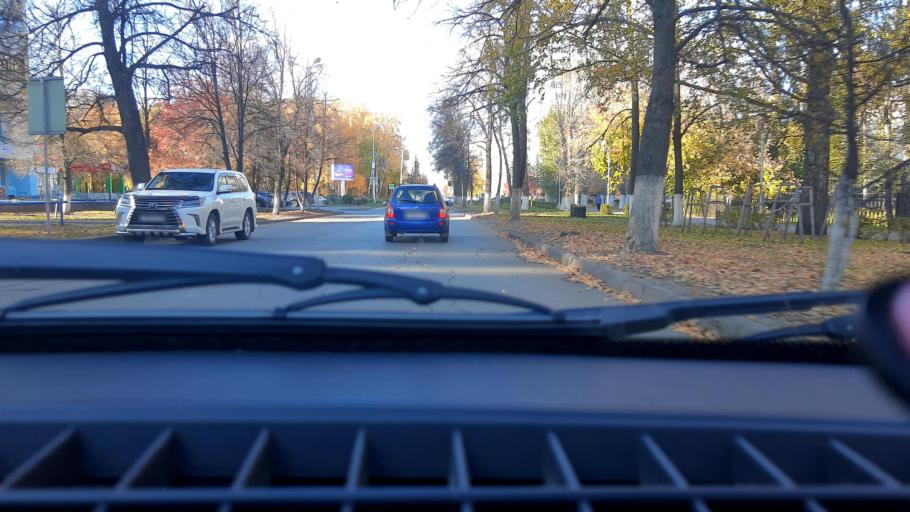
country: RU
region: Bashkortostan
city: Avdon
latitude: 54.7013
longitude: 55.8307
